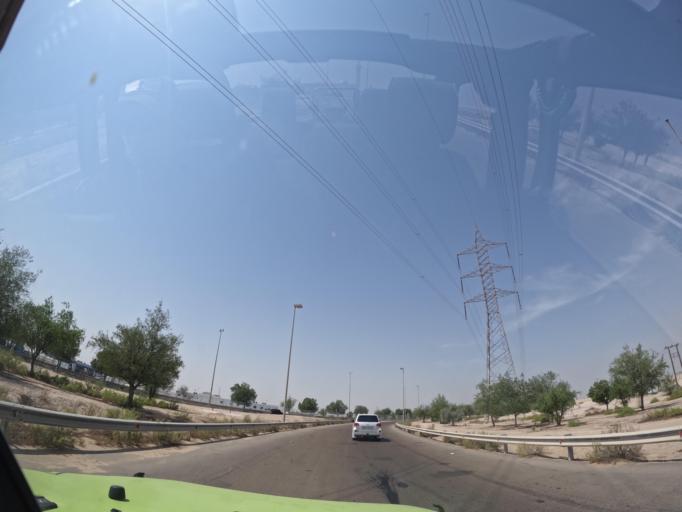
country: AE
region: Abu Dhabi
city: Abu Dhabi
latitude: 24.2193
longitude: 54.8529
